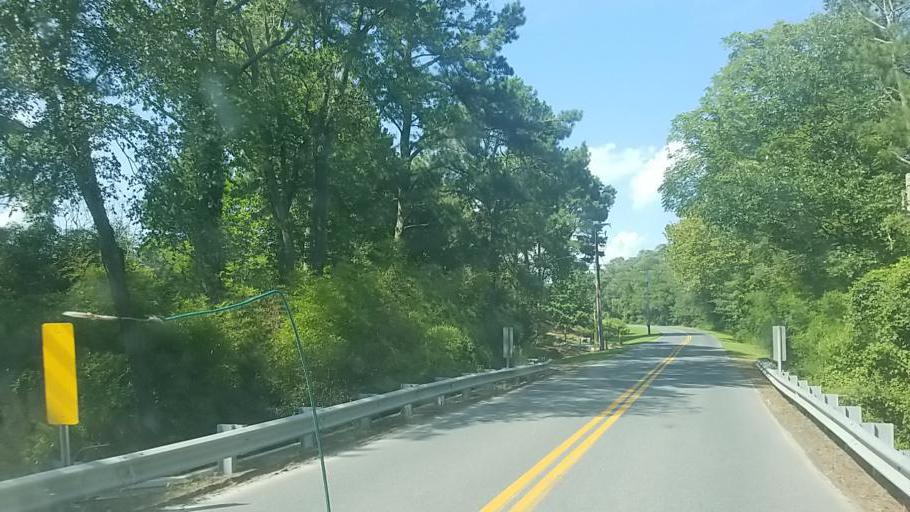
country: US
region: Maryland
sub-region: Somerset County
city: Princess Anne
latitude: 38.2641
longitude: -75.6808
